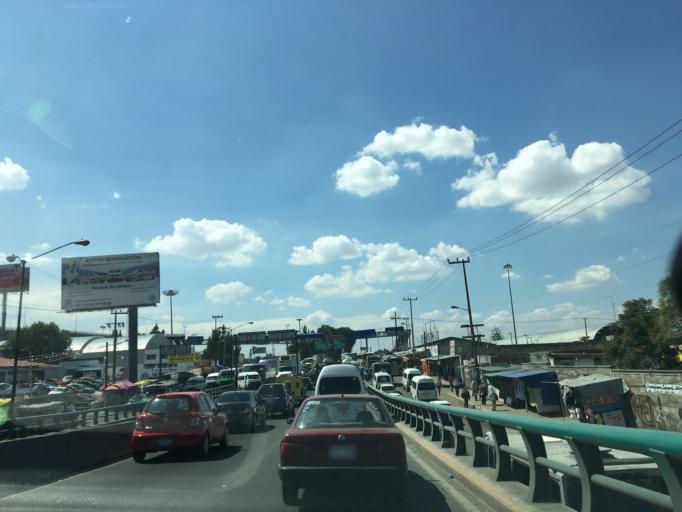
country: MX
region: Mexico
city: Los Reyes La Paz
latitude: 19.3589
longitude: -98.9927
